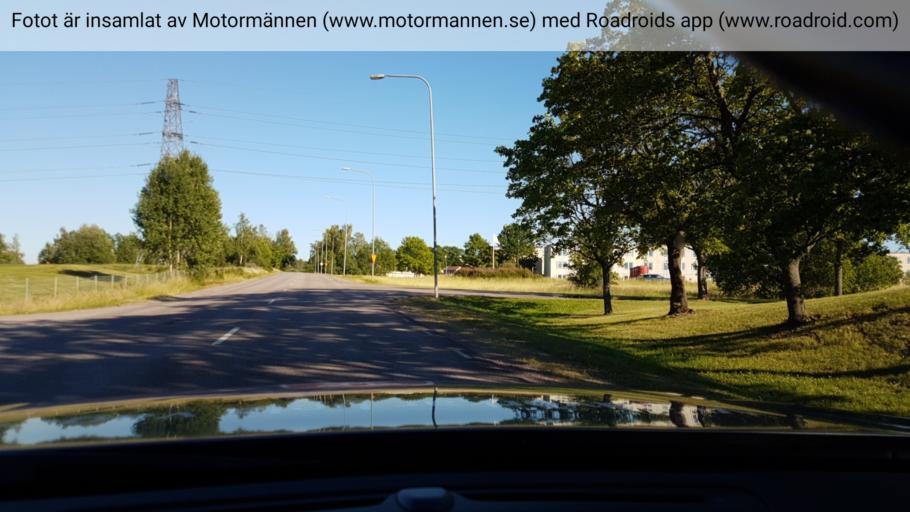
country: SE
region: Vaestmanland
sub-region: Vasteras
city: Vasteras
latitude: 59.6269
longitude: 16.5044
